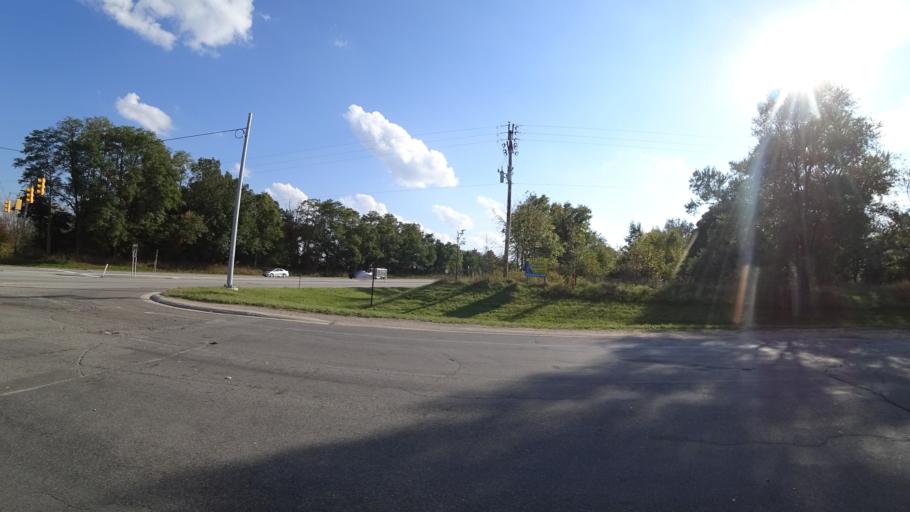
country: US
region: Michigan
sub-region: Saint Joseph County
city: Three Rivers
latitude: 41.9542
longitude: -85.6471
